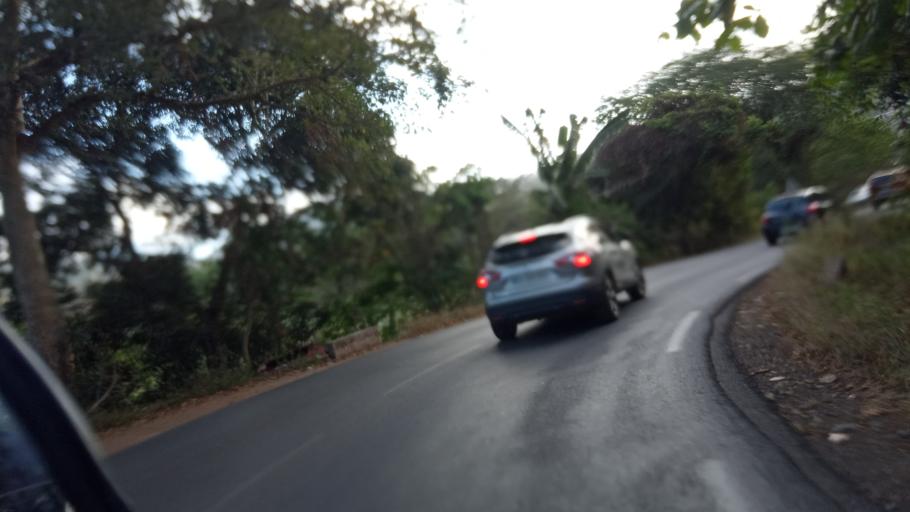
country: YT
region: Dembeni
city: Dembeni
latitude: -12.8366
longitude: 45.1791
